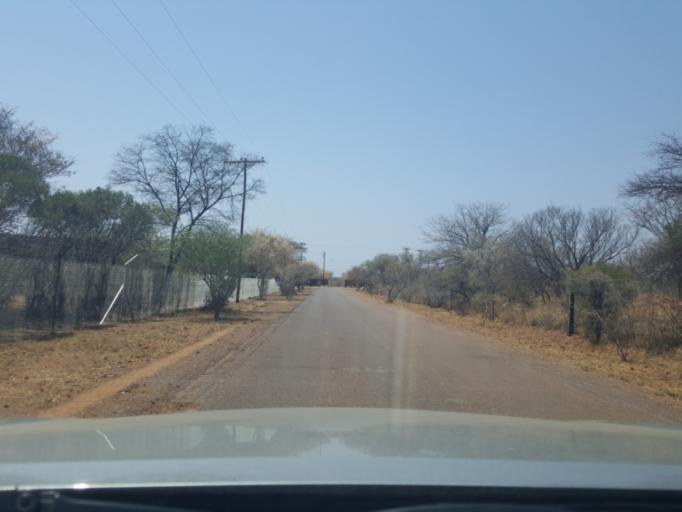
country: BW
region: South East
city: Ramotswa
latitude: -24.7632
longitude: 25.8439
